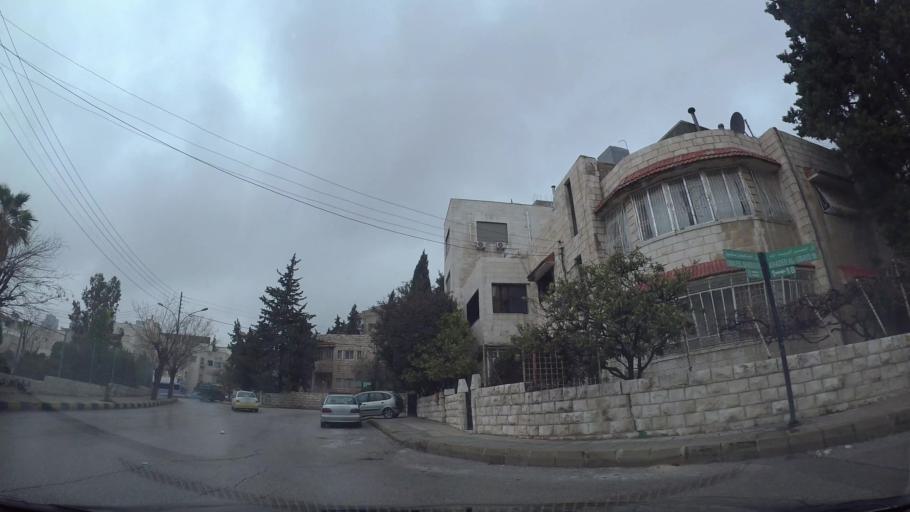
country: JO
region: Amman
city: Amman
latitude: 31.9635
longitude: 35.9205
